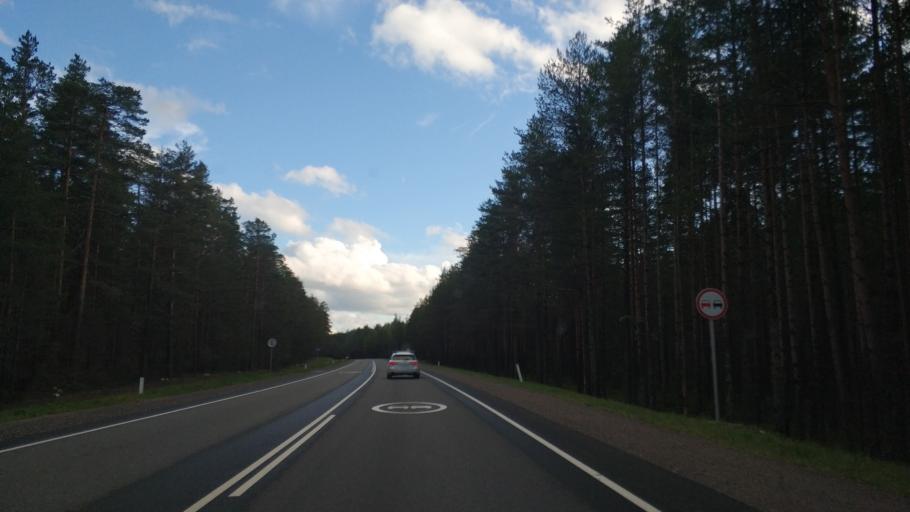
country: RU
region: Leningrad
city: Priozersk
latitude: 60.9877
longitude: 30.1833
